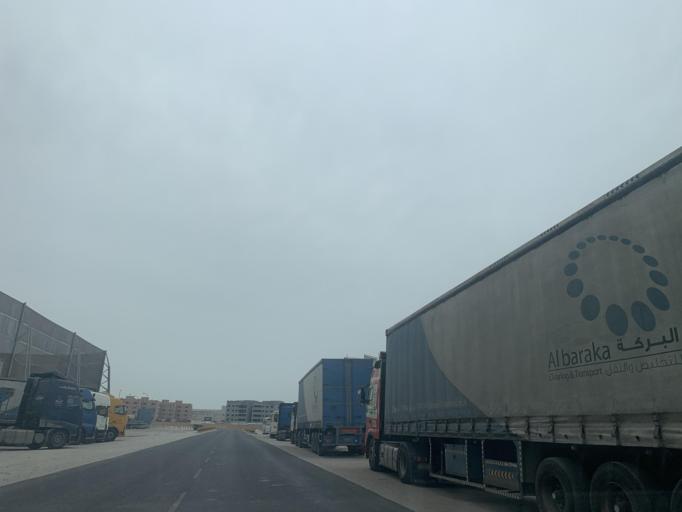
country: BH
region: Muharraq
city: Al Hadd
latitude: 26.2067
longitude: 50.6802
